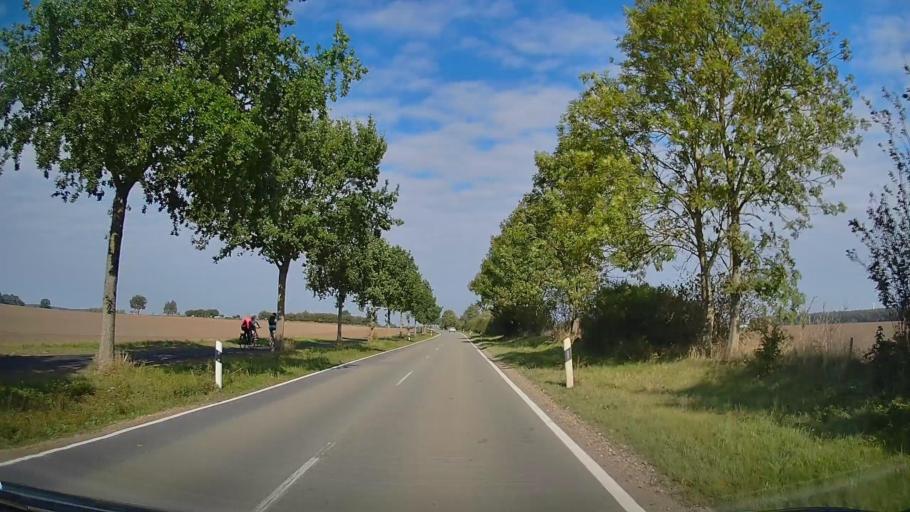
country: DE
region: Schleswig-Holstein
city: Oldenburg in Holstein
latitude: 54.3055
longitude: 10.8870
